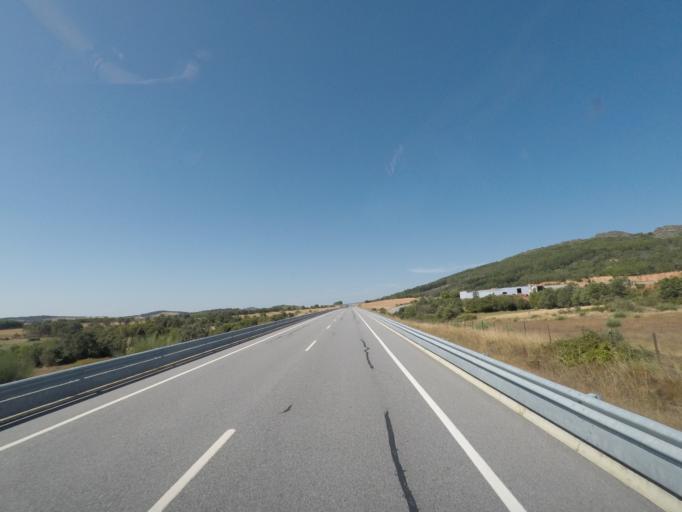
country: PT
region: Braganca
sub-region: Mogadouro
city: Mogadouro
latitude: 41.3489
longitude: -6.6086
